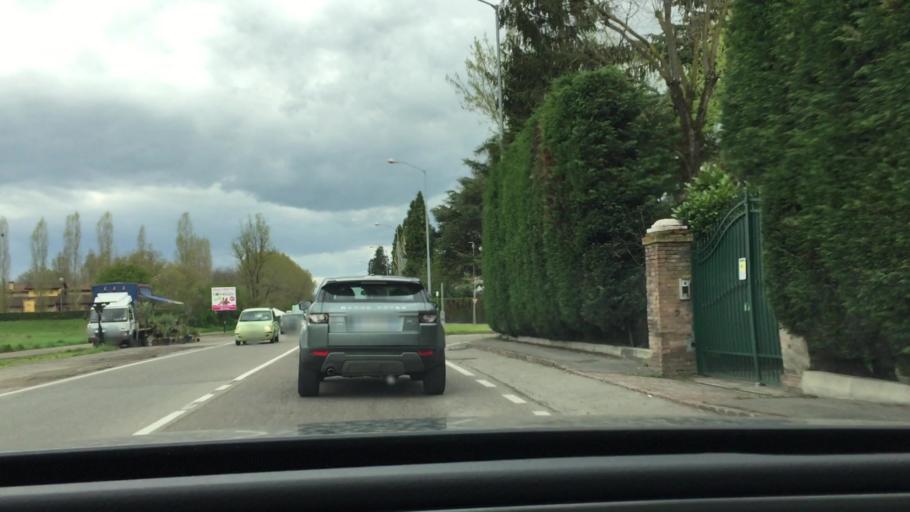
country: IT
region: Emilia-Romagna
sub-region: Provincia di Modena
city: Modena
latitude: 44.6272
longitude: 10.8963
